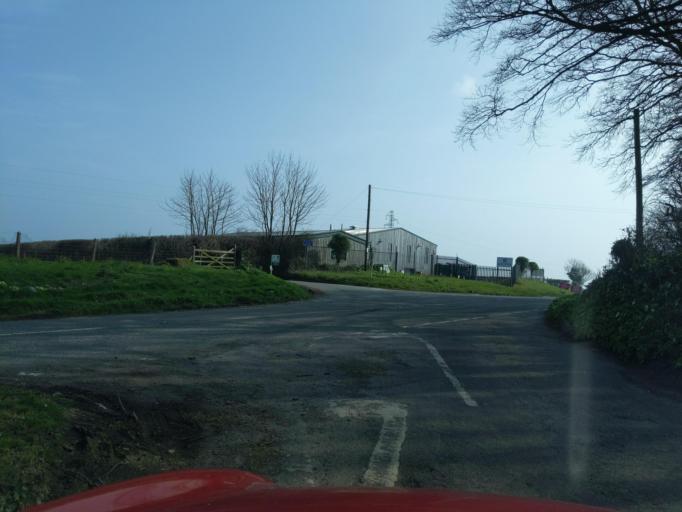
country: GB
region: England
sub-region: Devon
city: Kingsbridge
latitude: 50.3085
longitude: -3.7689
